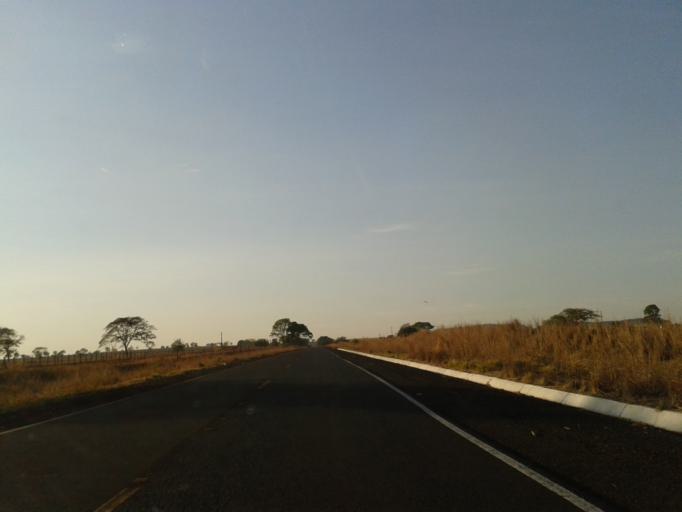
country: BR
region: Minas Gerais
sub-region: Santa Vitoria
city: Santa Vitoria
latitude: -19.1043
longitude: -50.3268
